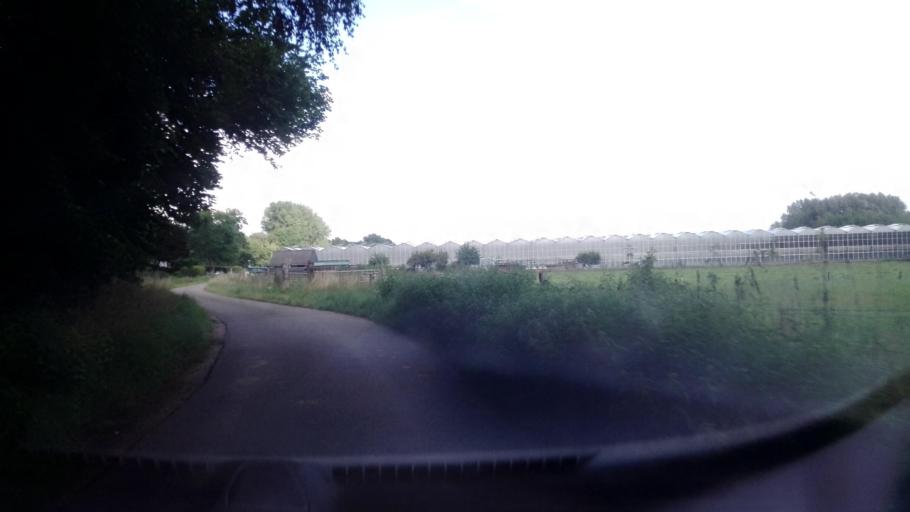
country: NL
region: Limburg
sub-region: Gemeente Venlo
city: Tegelen
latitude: 51.3611
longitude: 6.1007
